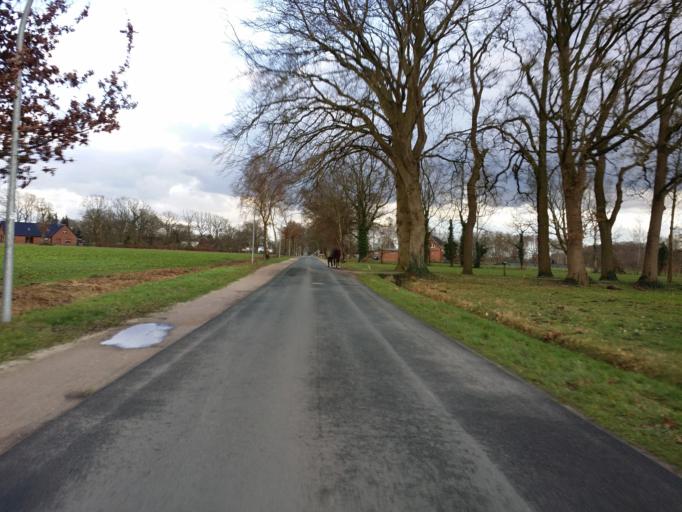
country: DE
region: Lower Saxony
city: Delmenhorst
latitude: 53.0138
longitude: 8.6403
